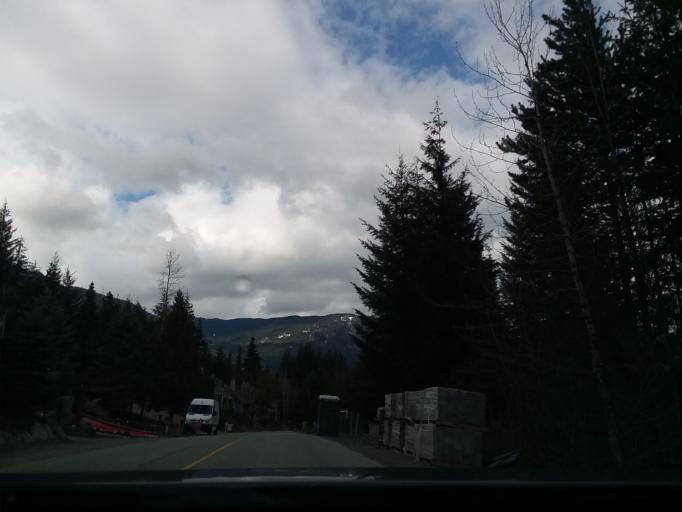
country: CA
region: British Columbia
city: Whistler
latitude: 50.1164
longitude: -122.9694
